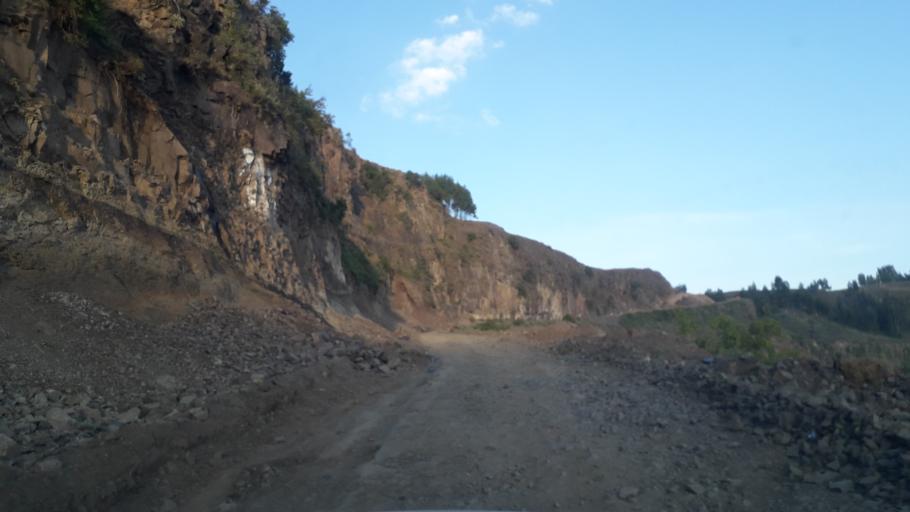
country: ET
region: Amhara
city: Lalibela
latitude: 11.5534
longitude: 39.2173
